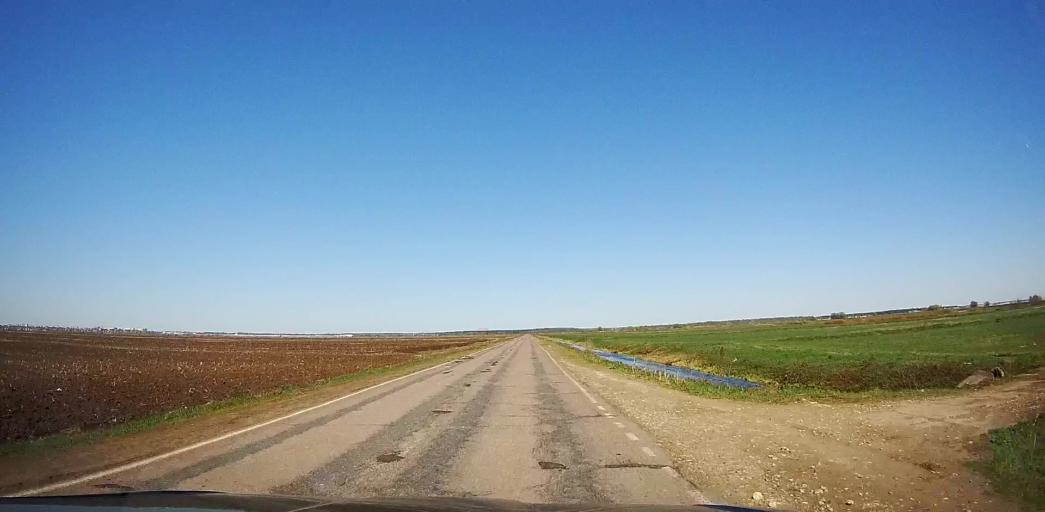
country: RU
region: Moskovskaya
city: Ramenskoye
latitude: 55.5061
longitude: 38.2512
